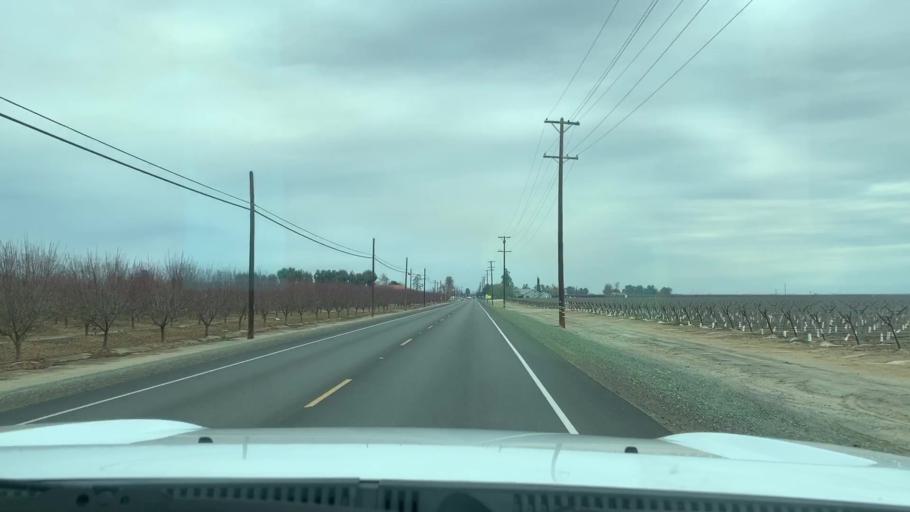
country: US
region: California
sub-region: Kern County
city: Shafter
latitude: 35.4150
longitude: -119.2519
